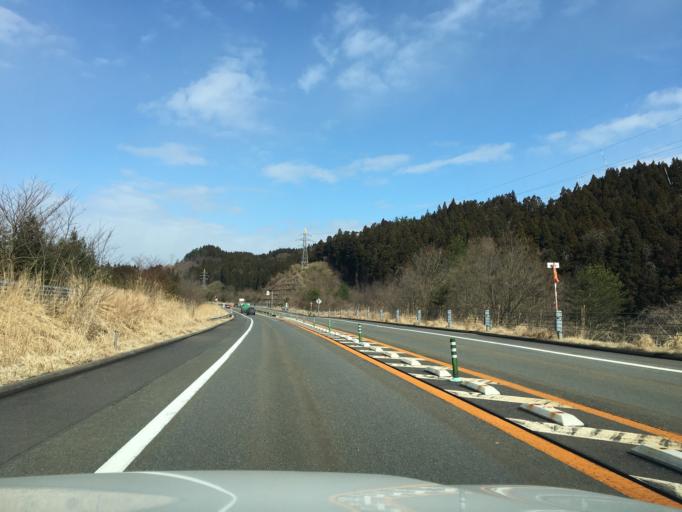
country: JP
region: Akita
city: Akita
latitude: 39.7732
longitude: 140.1203
